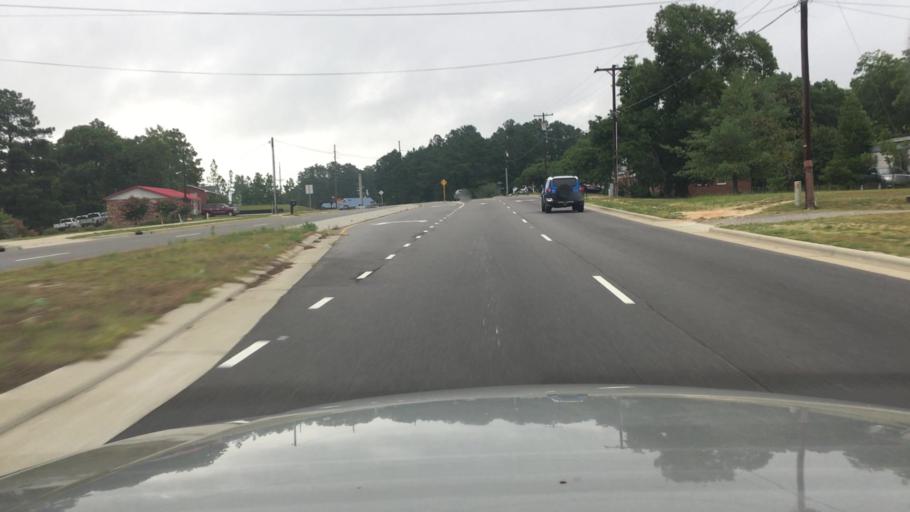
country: US
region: North Carolina
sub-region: Cumberland County
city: Hope Mills
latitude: 34.9858
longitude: -78.9275
